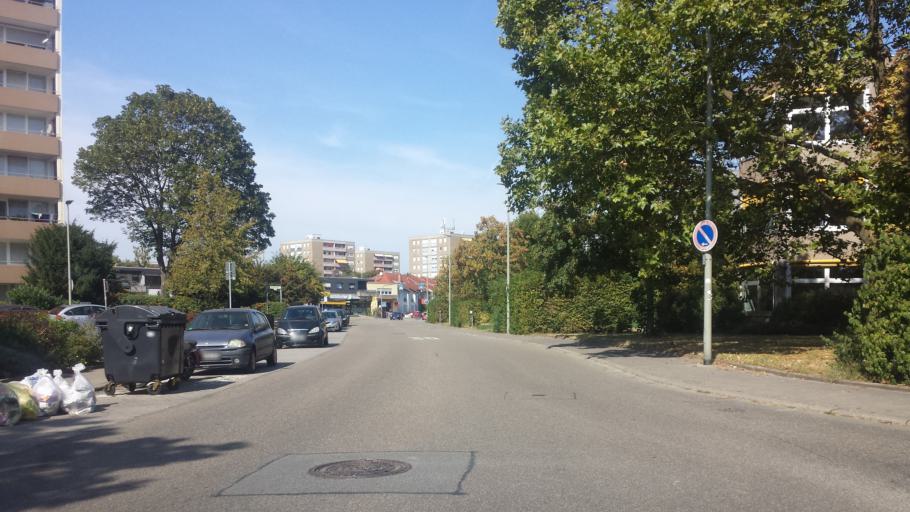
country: DE
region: Rheinland-Pfalz
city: Mutterstadt
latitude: 49.4379
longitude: 8.3522
